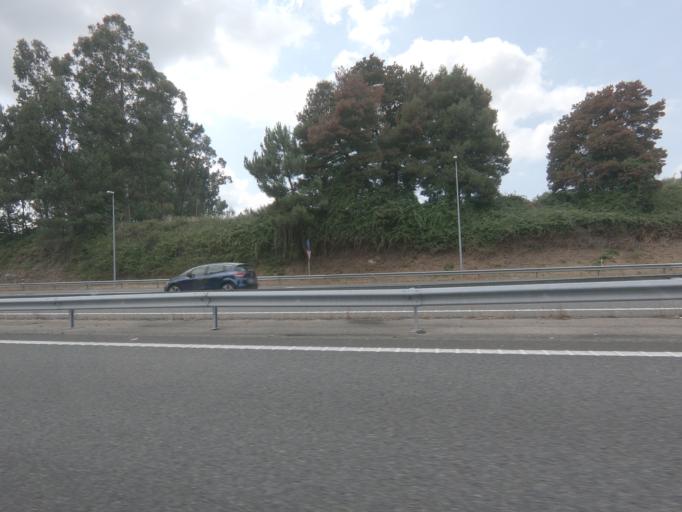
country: ES
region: Galicia
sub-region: Provincia de Pontevedra
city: Tui
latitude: 42.0501
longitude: -8.6557
